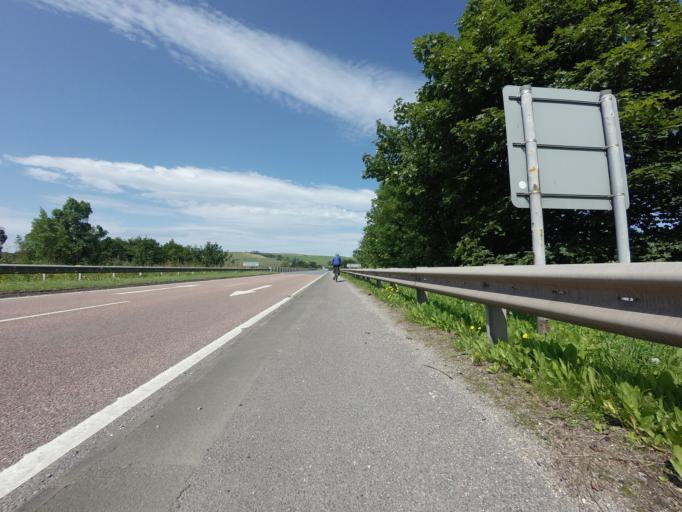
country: GB
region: Scotland
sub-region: Highland
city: Conon Bridge
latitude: 57.5729
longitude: -4.4299
